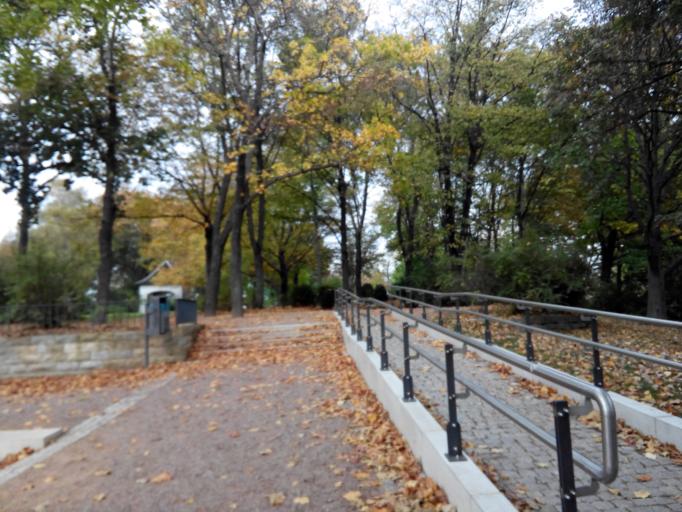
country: DE
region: Thuringia
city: Erfurt
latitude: 50.9702
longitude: 11.0398
